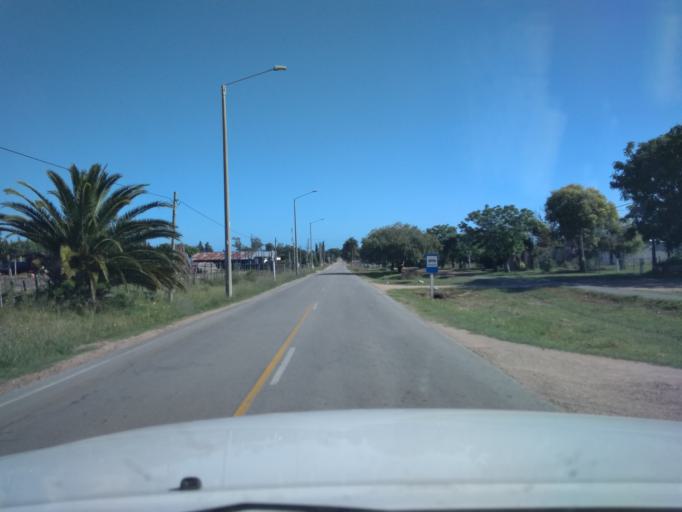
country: UY
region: Canelones
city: San Ramon
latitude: -34.3021
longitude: -55.9580
